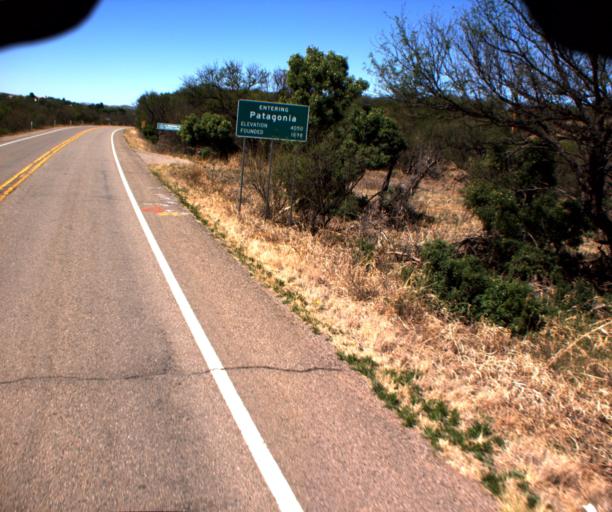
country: US
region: Arizona
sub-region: Santa Cruz County
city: Rio Rico
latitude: 31.5484
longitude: -110.7409
